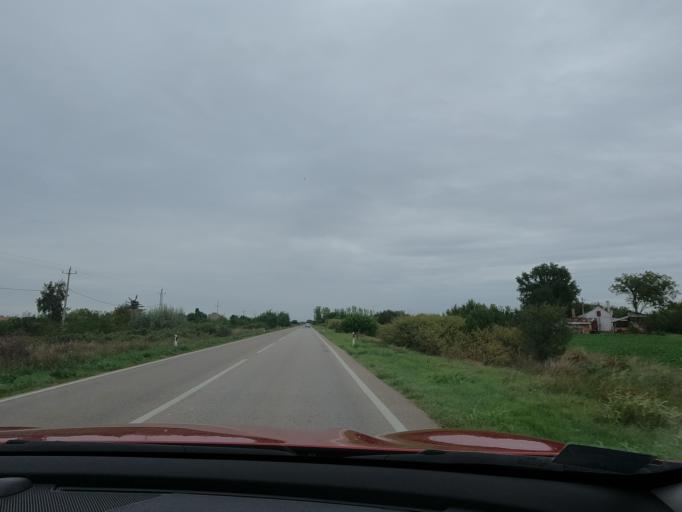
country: RS
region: Autonomna Pokrajina Vojvodina
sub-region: Severnobanatski Okrug
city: Kikinda
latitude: 45.7701
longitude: 20.4245
